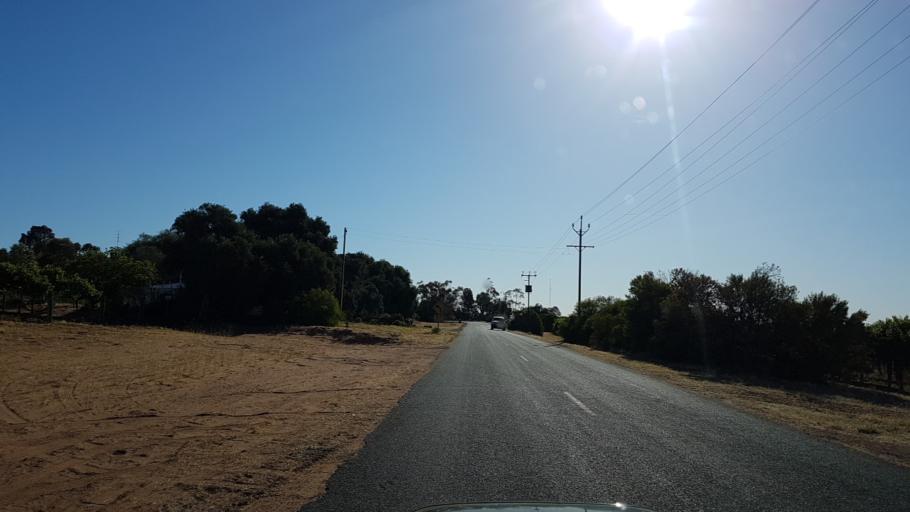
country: AU
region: South Australia
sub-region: Loxton Waikerie
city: Waikerie
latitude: -34.1694
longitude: 140.0352
